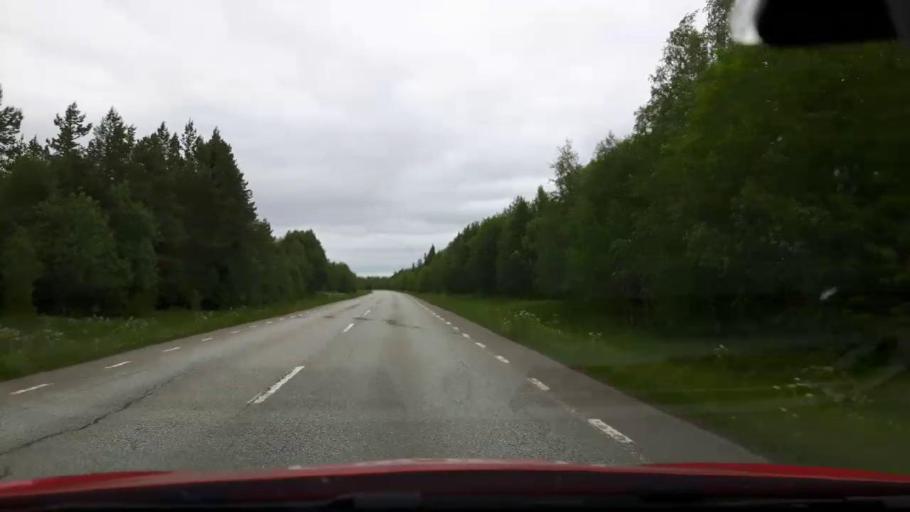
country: SE
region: Jaemtland
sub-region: OEstersunds Kommun
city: Lit
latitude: 63.5982
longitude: 14.6558
